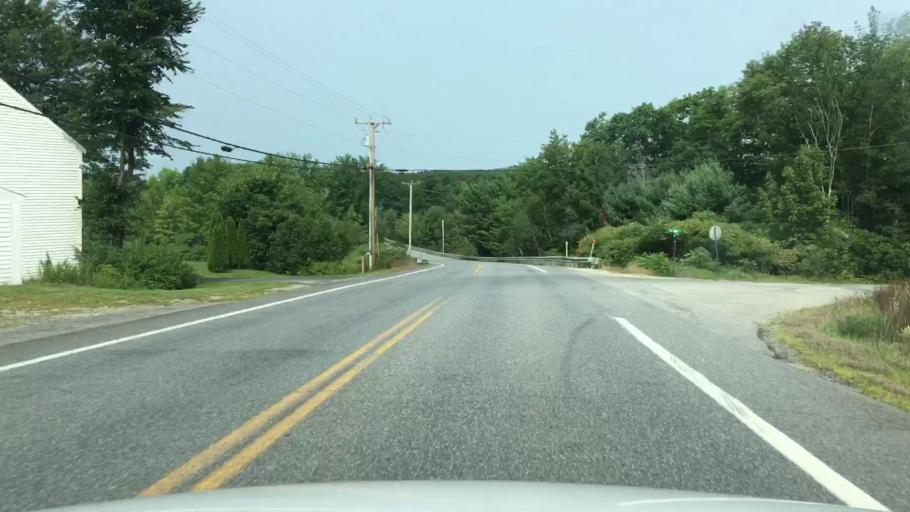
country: US
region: Maine
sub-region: Kennebec County
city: Winthrop
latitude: 44.3370
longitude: -70.0158
